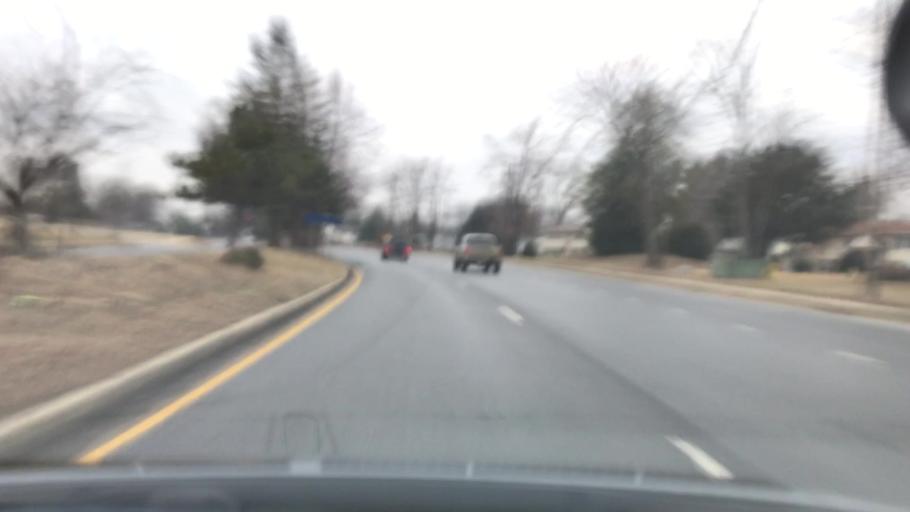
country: US
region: Maryland
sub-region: Anne Arundel County
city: Arnold
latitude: 39.0538
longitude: -76.5096
